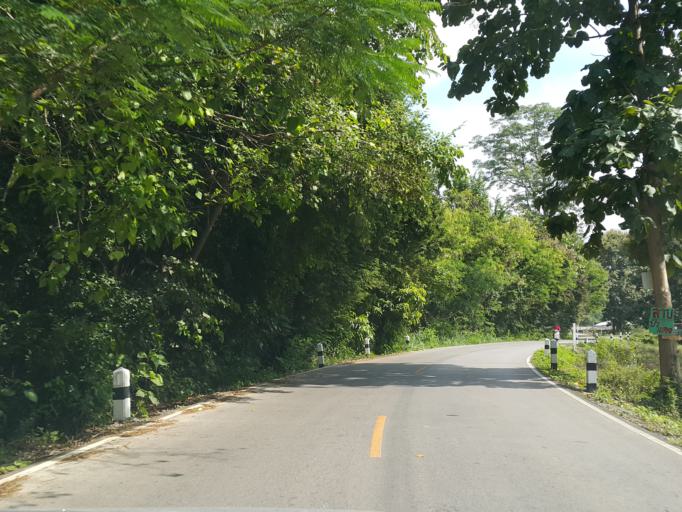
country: TH
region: Chiang Mai
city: San Sai
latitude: 18.8990
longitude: 99.0187
